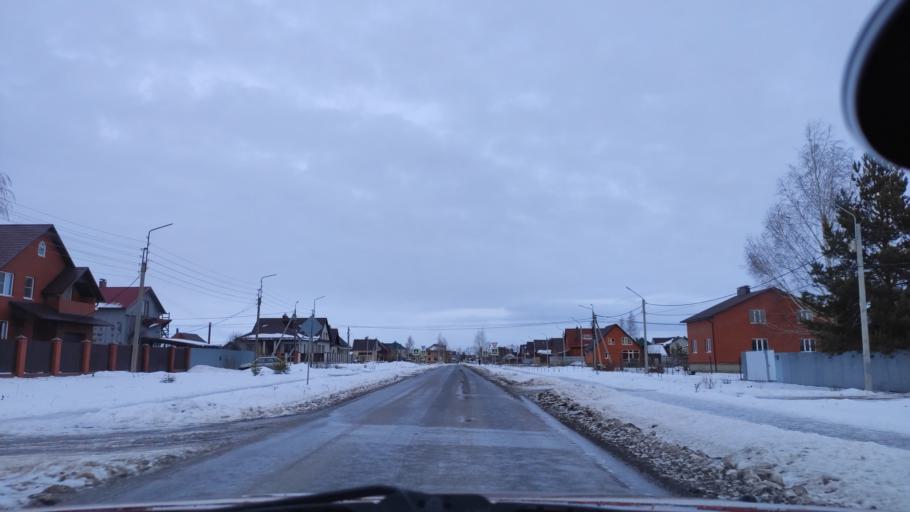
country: RU
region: Tambov
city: Tambov
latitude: 52.7637
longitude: 41.3748
